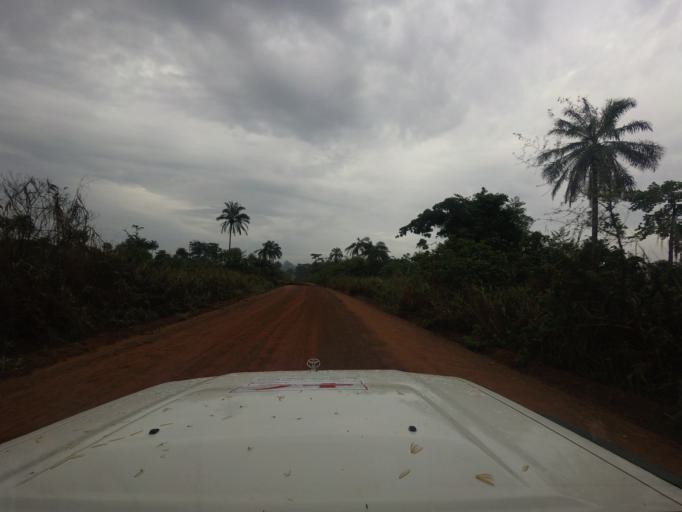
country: LR
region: Lofa
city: Voinjama
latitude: 8.4024
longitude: -9.7840
